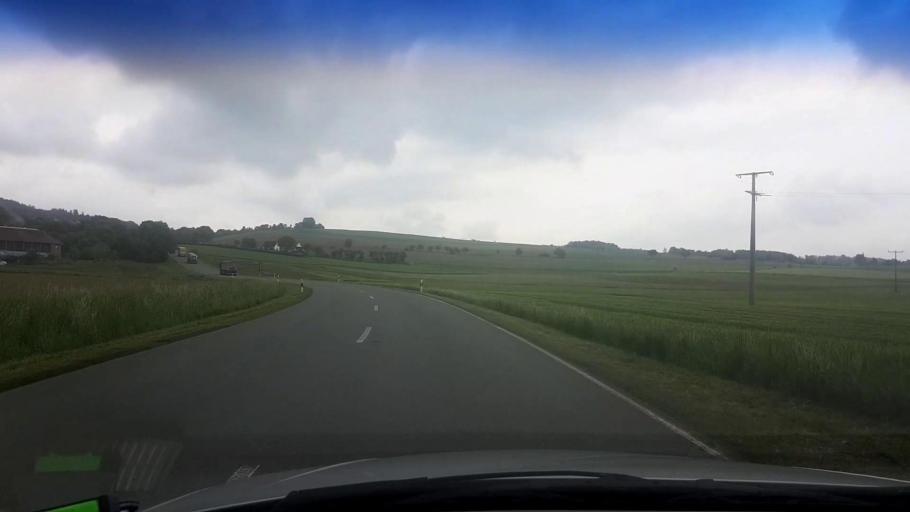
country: DE
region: Bavaria
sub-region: Upper Franconia
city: Reuth
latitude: 49.9950
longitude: 11.6796
